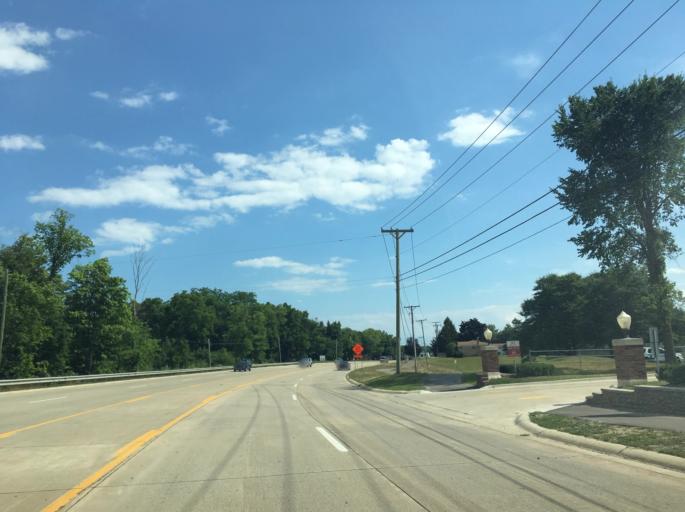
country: US
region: Michigan
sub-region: Macomb County
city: Clinton
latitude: 42.6178
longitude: -82.9336
